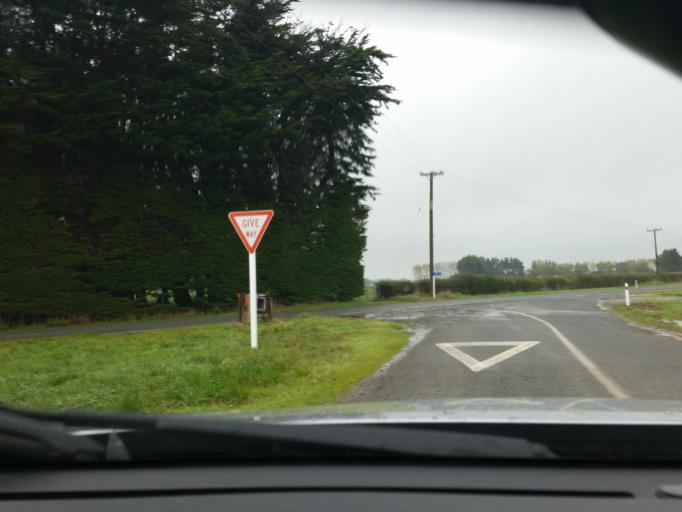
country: NZ
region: Southland
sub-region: Invercargill City
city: Invercargill
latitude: -46.3093
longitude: 168.3033
